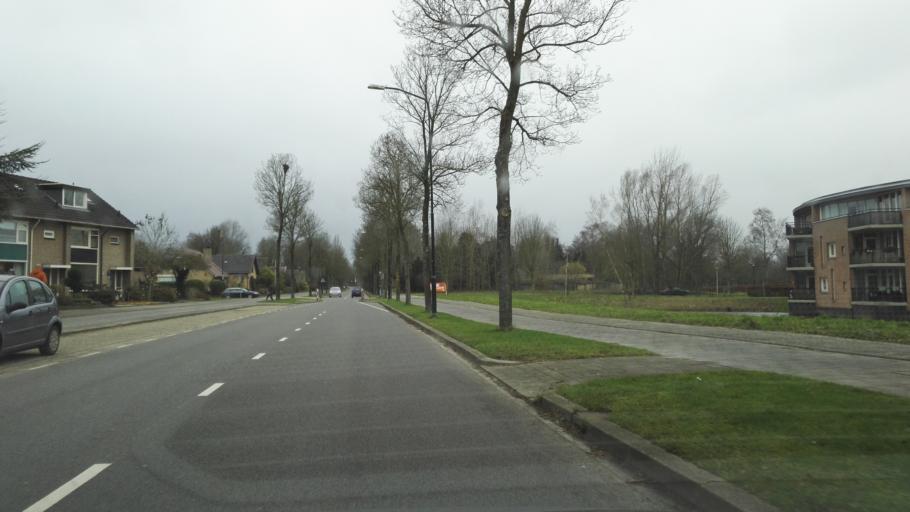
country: NL
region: Gelderland
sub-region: Gemeente Apeldoorn
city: Apeldoorn
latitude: 52.2338
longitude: 5.9853
